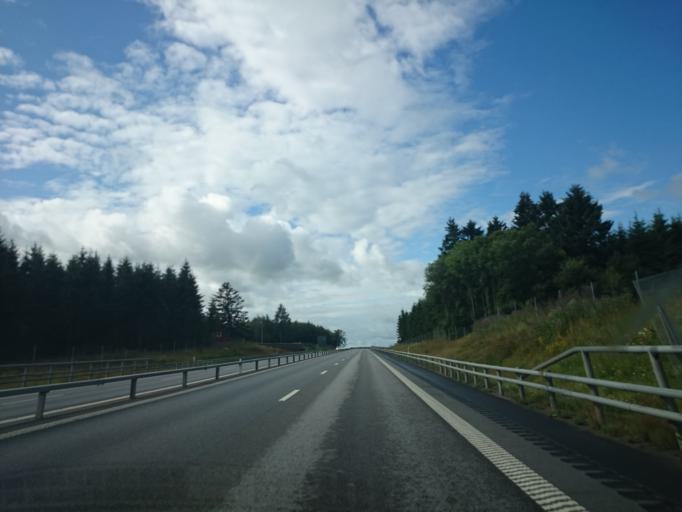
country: SE
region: Skane
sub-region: Horby Kommun
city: Hoerby
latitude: 55.8823
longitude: 13.7143
